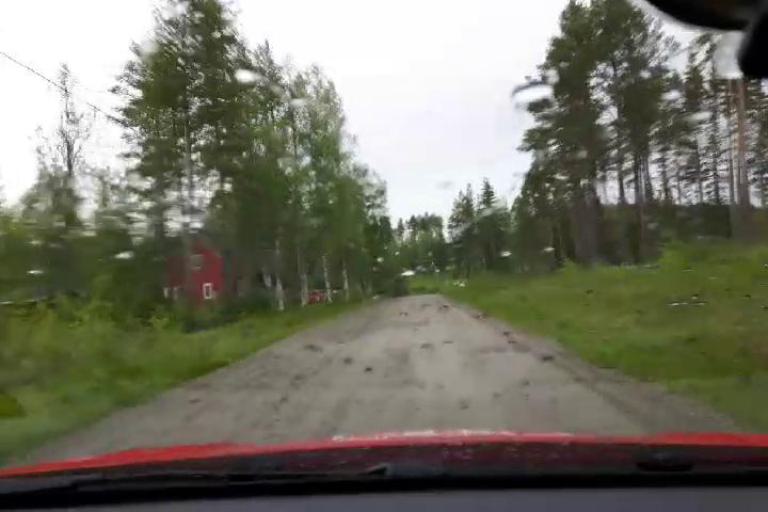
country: SE
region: Jaemtland
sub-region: Bergs Kommun
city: Hoverberg
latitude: 62.7473
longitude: 14.4498
